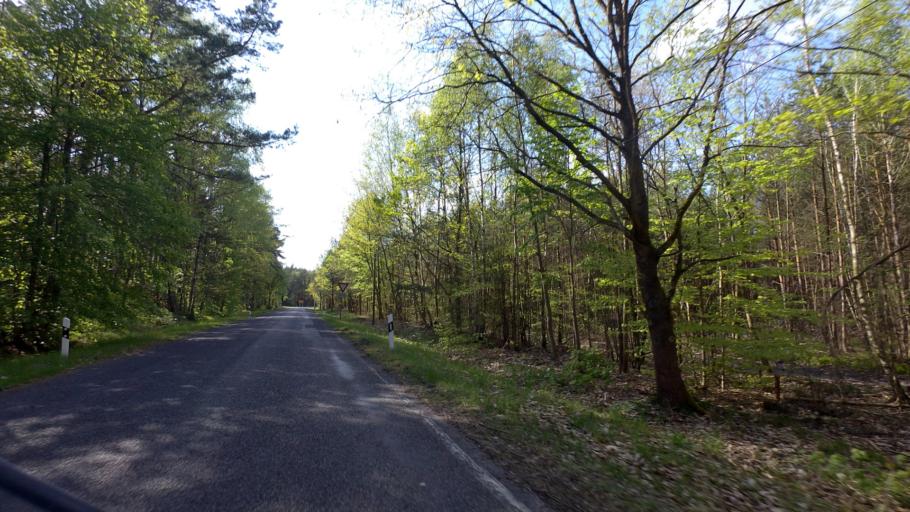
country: DE
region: Brandenburg
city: Zehdenick
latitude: 53.0185
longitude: 13.3748
